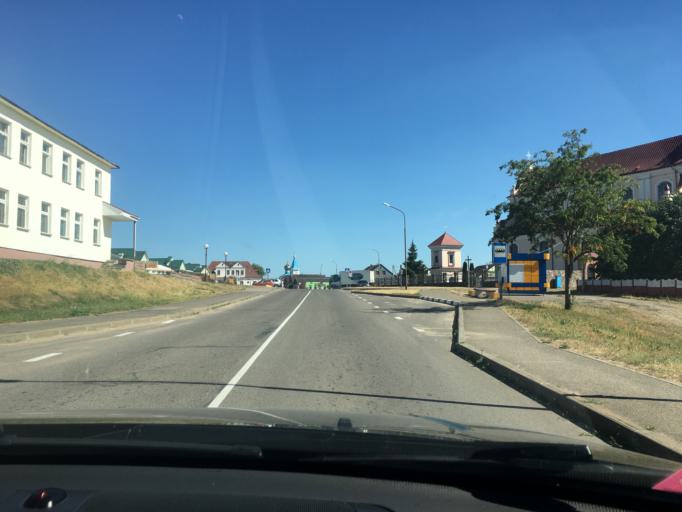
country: BY
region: Grodnenskaya
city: Hal'shany
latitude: 54.2579
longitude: 26.0095
